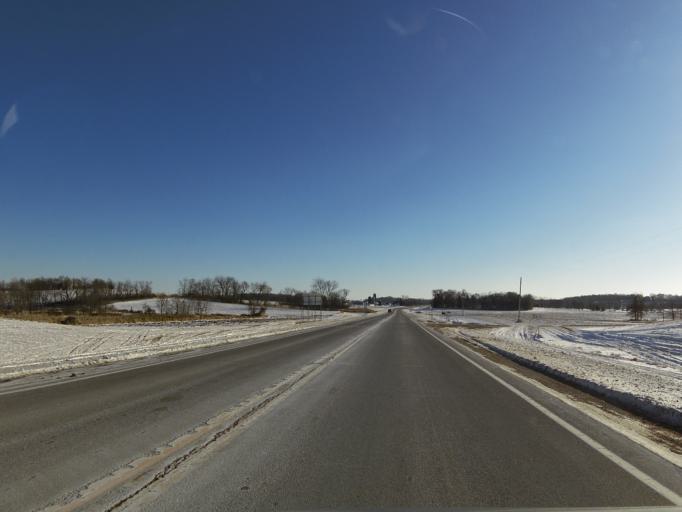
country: US
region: Minnesota
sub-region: Le Sueur County
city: New Prague
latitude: 44.5711
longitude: -93.5044
